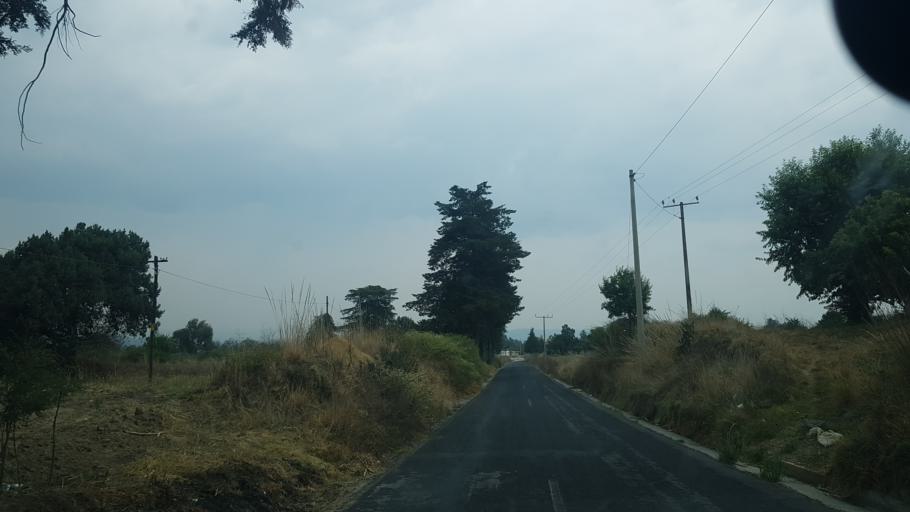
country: MX
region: Puebla
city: San Lorenzo Chiautzingo
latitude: 19.1937
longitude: -98.4686
